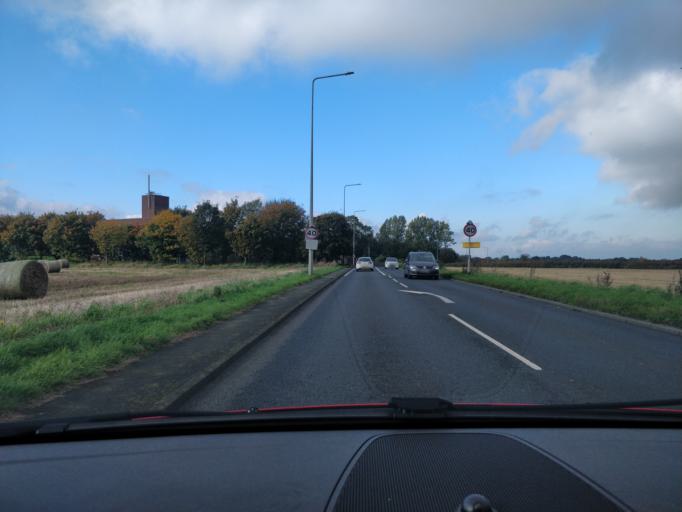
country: GB
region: England
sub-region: Lancashire
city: Ormskirk
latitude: 53.5924
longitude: -2.9202
